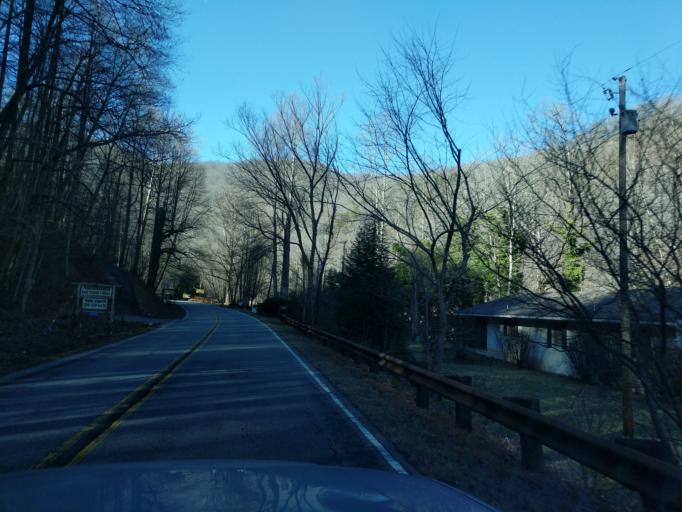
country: US
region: North Carolina
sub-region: Swain County
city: Bryson City
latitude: 35.3338
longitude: -83.6129
